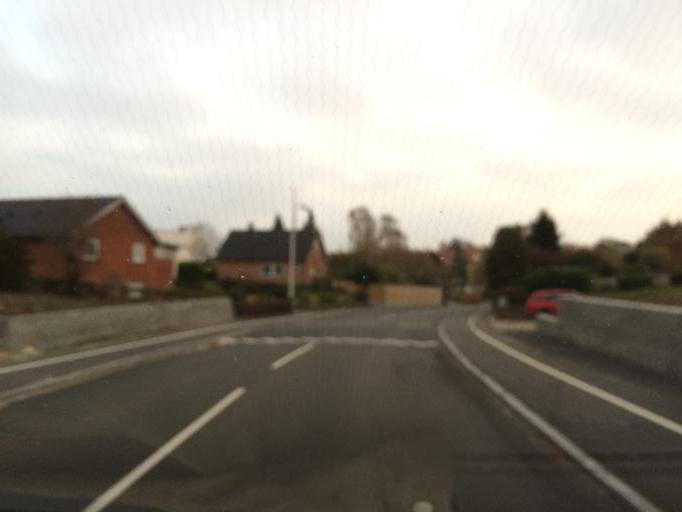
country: DK
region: Central Jutland
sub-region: Silkeborg Kommune
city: Silkeborg
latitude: 56.1837
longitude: 9.5221
